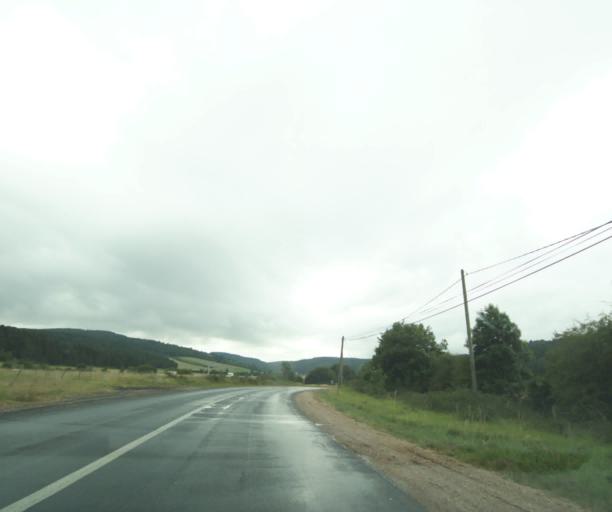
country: FR
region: Midi-Pyrenees
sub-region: Departement de l'Aveyron
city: Severac-le-Chateau
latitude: 44.3833
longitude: 3.1162
